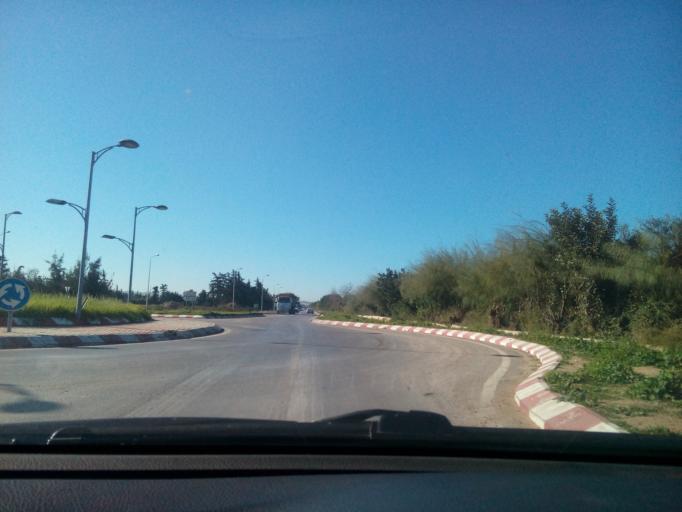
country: DZ
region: Relizane
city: Relizane
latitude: 35.7220
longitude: 0.5076
